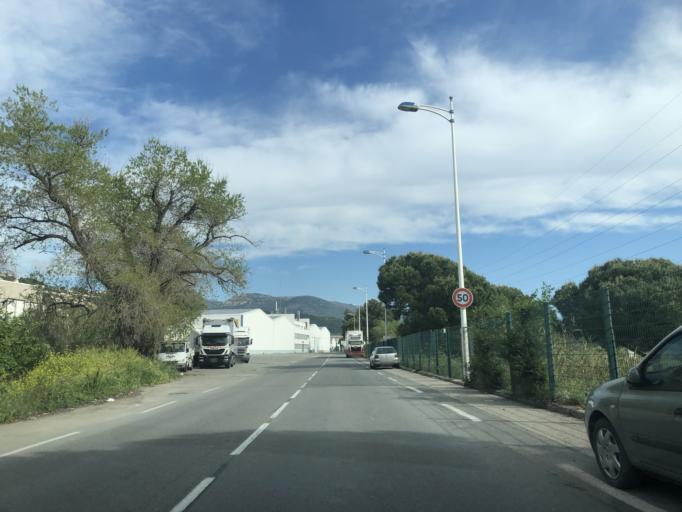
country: FR
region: Provence-Alpes-Cote d'Azur
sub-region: Departement des Alpes-Maritimes
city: Saint-Laurent-du-Var
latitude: 43.6924
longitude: 7.1854
